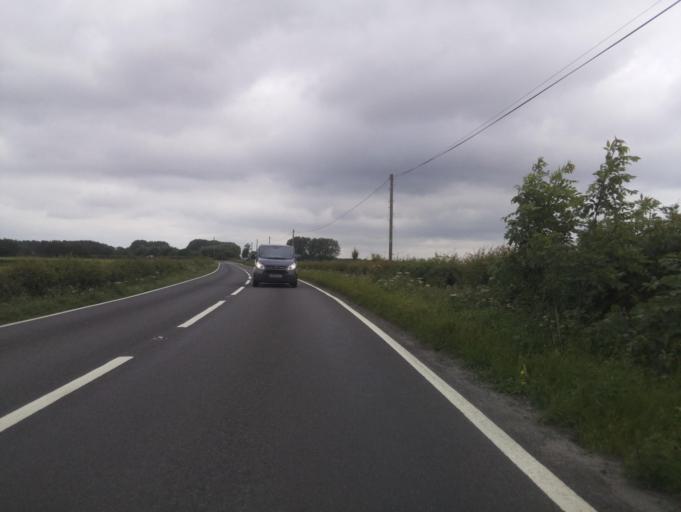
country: GB
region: England
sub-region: Staffordshire
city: Mayfield
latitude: 52.9722
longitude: -1.7508
